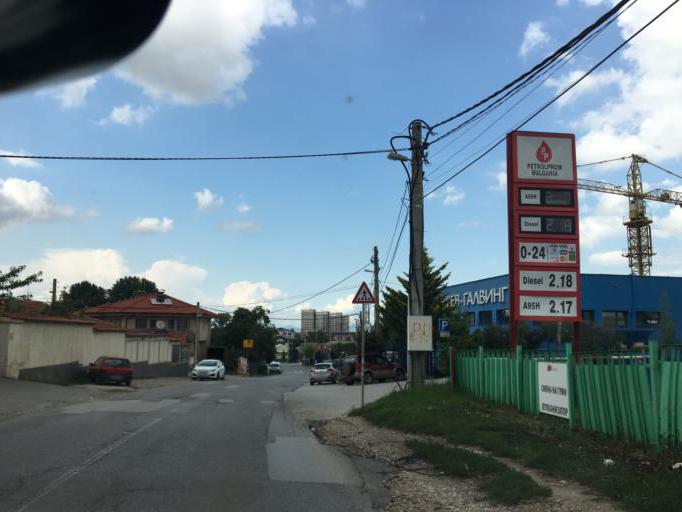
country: BG
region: Sofia-Capital
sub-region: Stolichna Obshtina
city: Sofia
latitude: 42.6390
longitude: 23.3532
